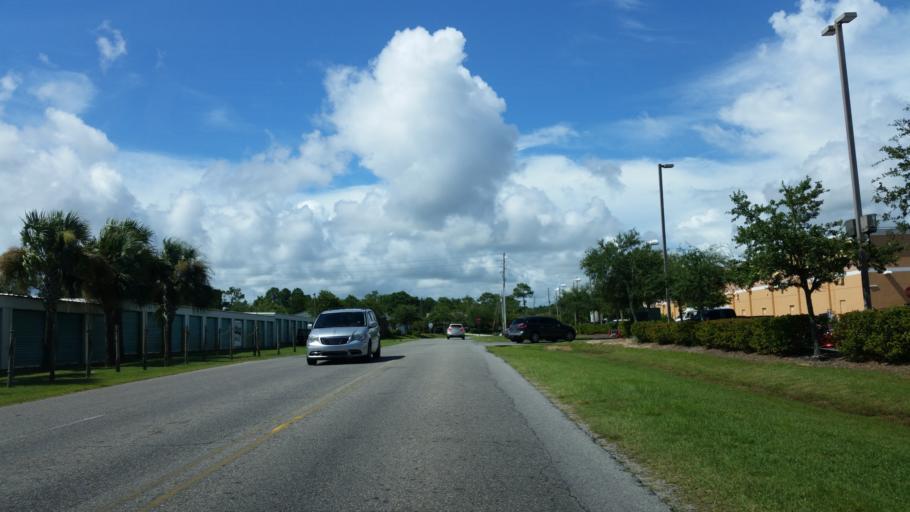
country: US
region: Florida
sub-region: Santa Rosa County
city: Navarre
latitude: 30.4021
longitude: -86.8797
